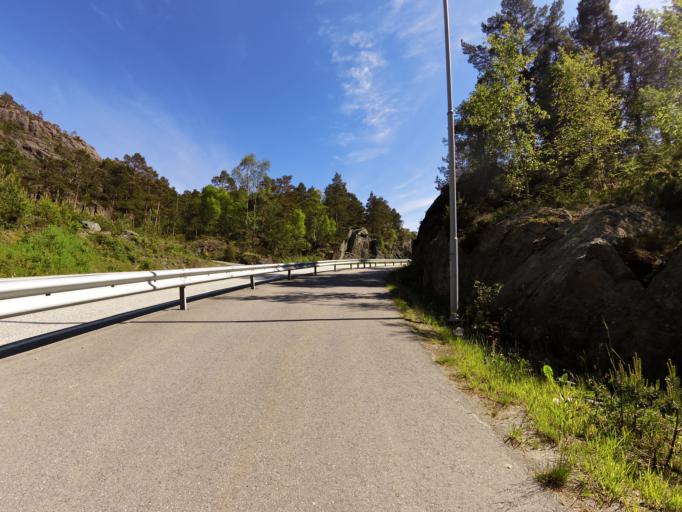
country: NO
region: Hordaland
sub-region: Stord
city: Sagvag
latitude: 59.7859
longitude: 5.3739
